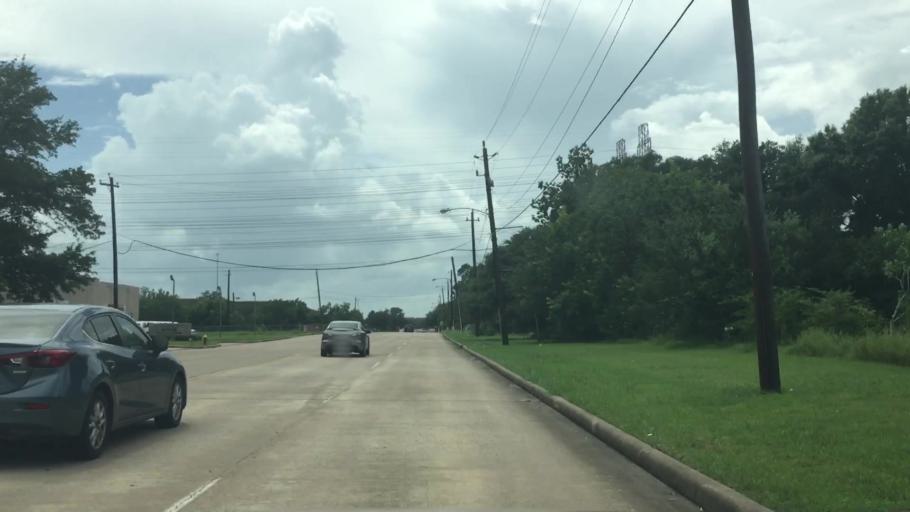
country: US
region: Texas
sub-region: Harris County
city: Webster
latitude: 29.5381
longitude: -95.1307
